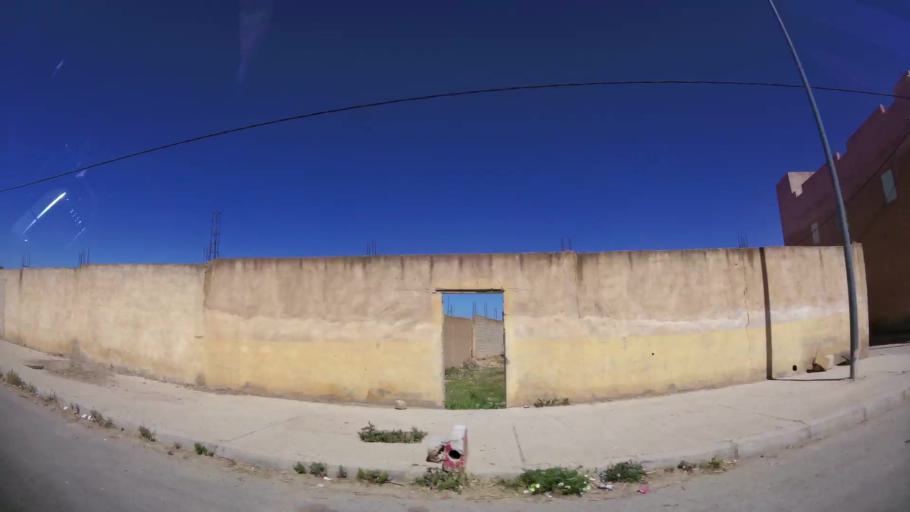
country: MA
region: Oriental
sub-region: Oujda-Angad
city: Oujda
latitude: 34.6952
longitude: -1.8568
